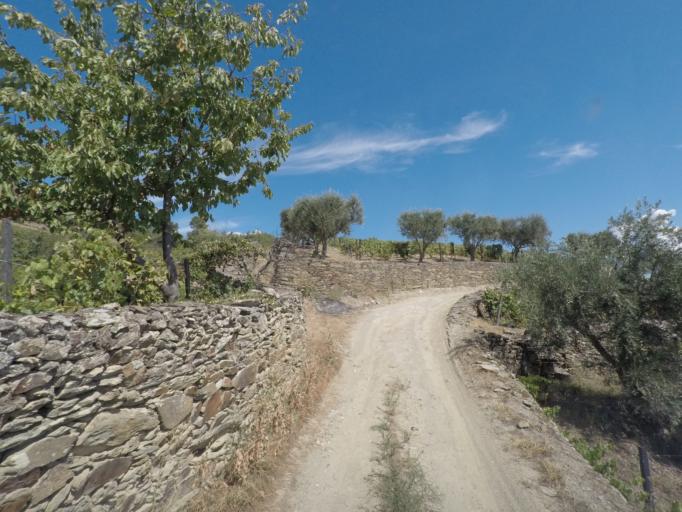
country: PT
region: Vila Real
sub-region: Sabrosa
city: Vilela
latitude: 41.1999
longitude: -7.5276
